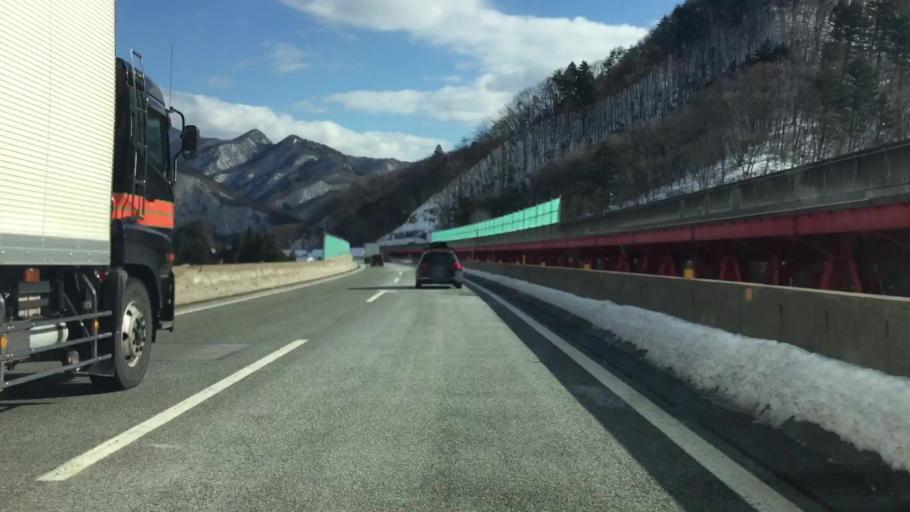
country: JP
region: Gunma
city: Numata
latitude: 36.7745
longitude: 138.9490
